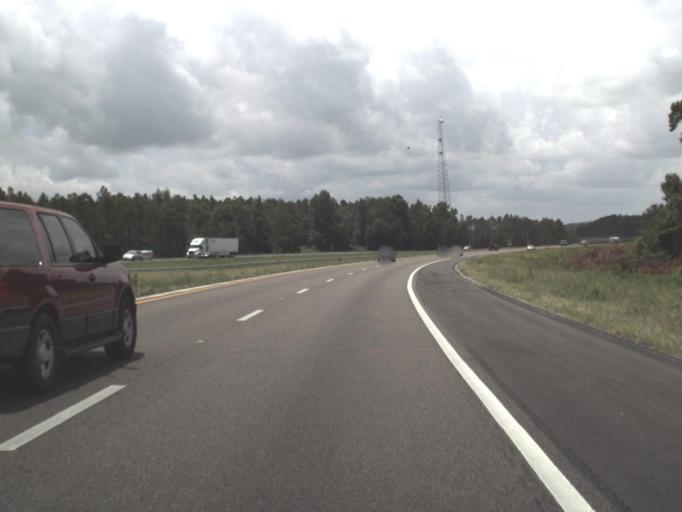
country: US
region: Florida
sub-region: Pasco County
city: San Antonio
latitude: 28.4245
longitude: -82.2834
